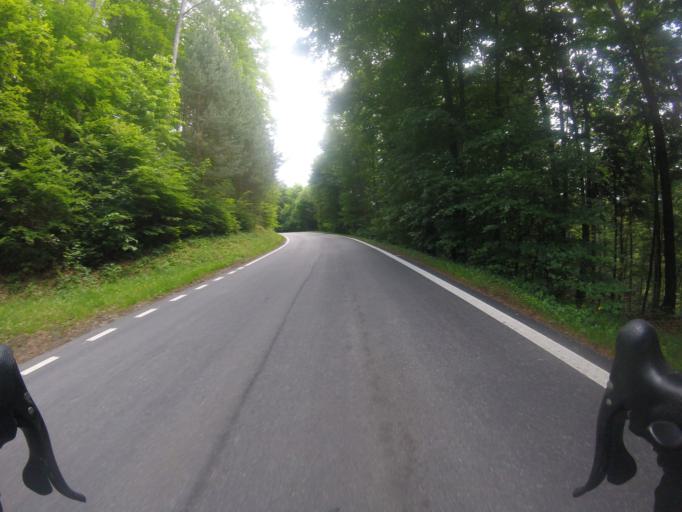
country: CH
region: Bern
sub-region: Bern-Mittelland District
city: Toffen
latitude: 46.8678
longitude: 7.5103
